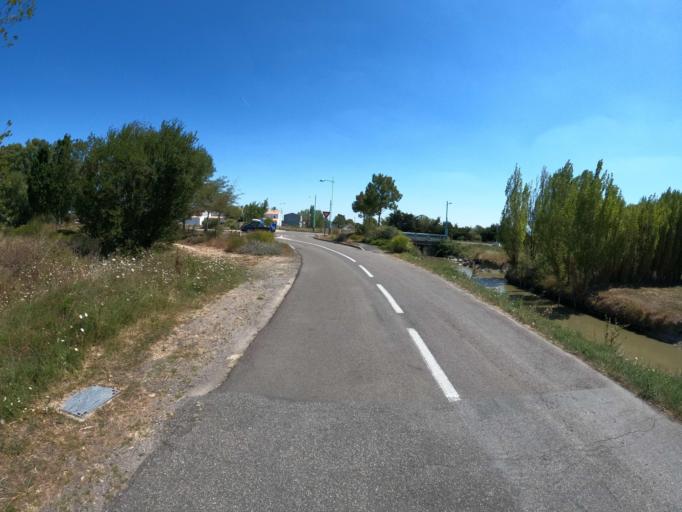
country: FR
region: Pays de la Loire
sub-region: Departement de la Vendee
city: Saint-Jean-de-Monts
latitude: 46.8000
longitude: -2.0685
